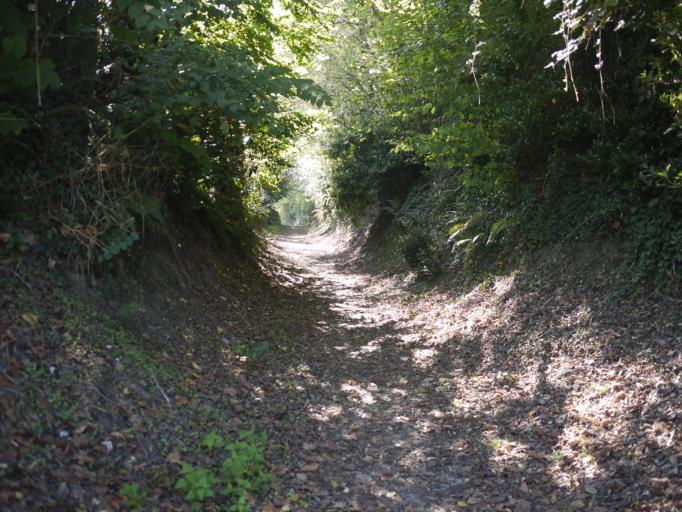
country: FR
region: Aquitaine
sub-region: Departement des Landes
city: Saint-Paul-les-Dax
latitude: 43.7250
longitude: -1.0644
